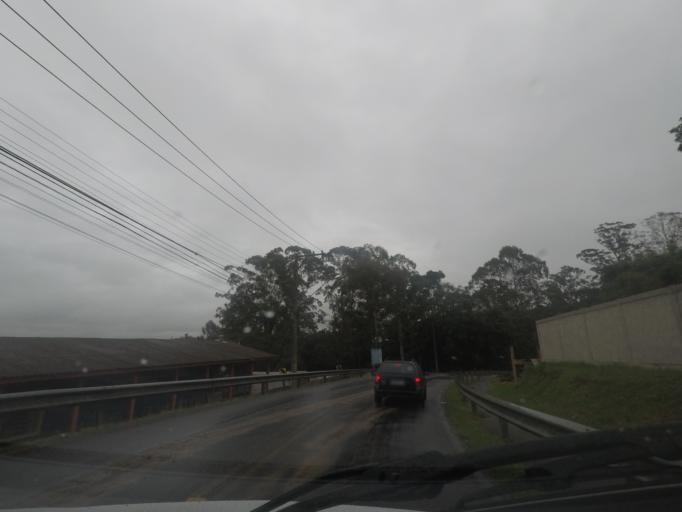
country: BR
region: Parana
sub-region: Quatro Barras
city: Quatro Barras
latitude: -25.3769
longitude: -49.1142
